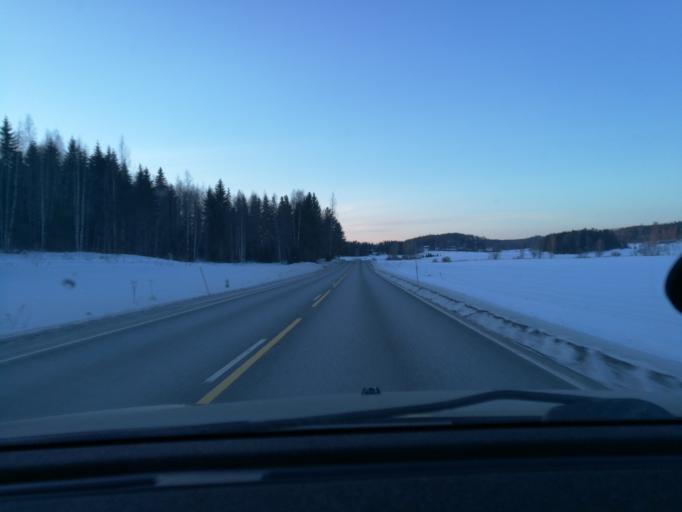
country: FI
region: Uusimaa
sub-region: Helsinki
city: Vihti
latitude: 60.4287
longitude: 24.4289
